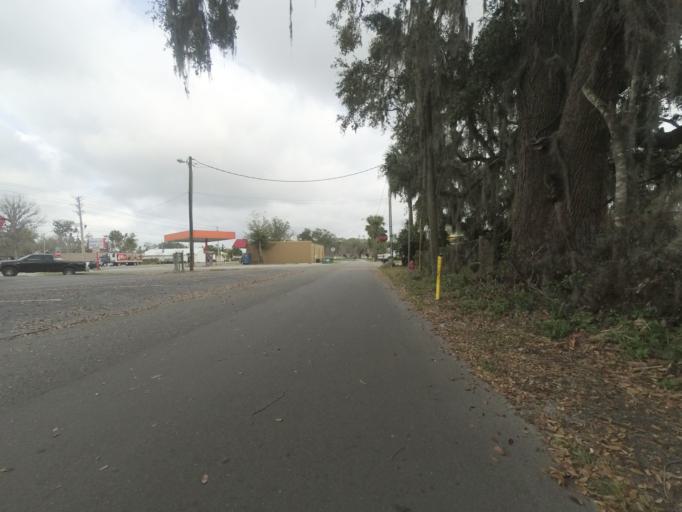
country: US
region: Florida
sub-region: Lake County
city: Umatilla
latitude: 28.9275
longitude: -81.6679
